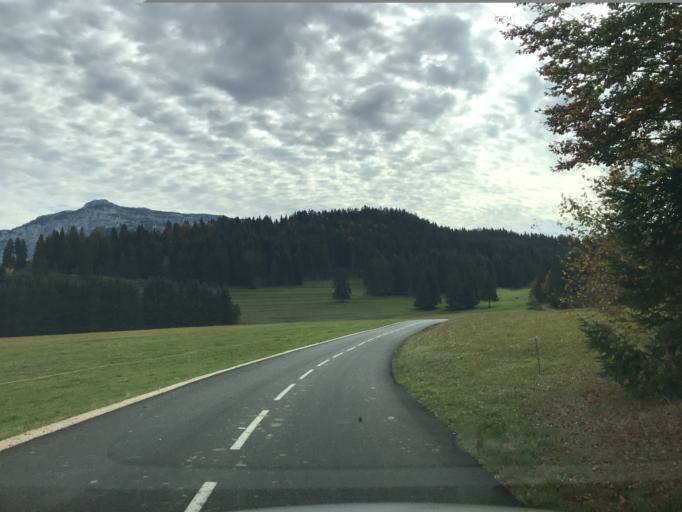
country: FR
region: Rhone-Alpes
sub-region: Departement de la Savoie
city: Vimines
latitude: 45.4564
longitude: 5.8582
